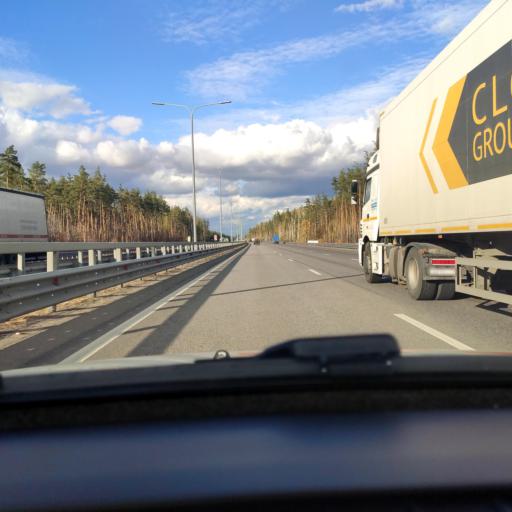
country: RU
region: Voronezj
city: Somovo
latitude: 51.7060
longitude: 39.3068
